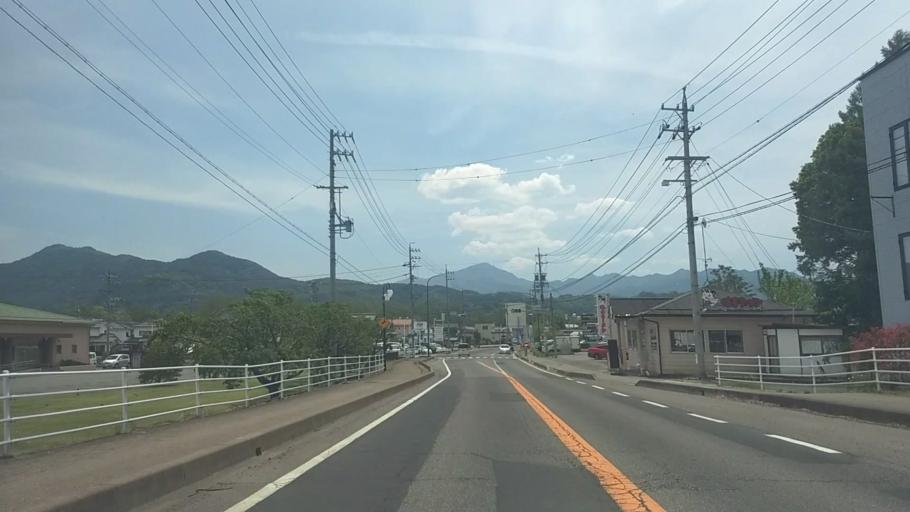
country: JP
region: Nagano
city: Saku
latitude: 36.1789
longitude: 138.4828
